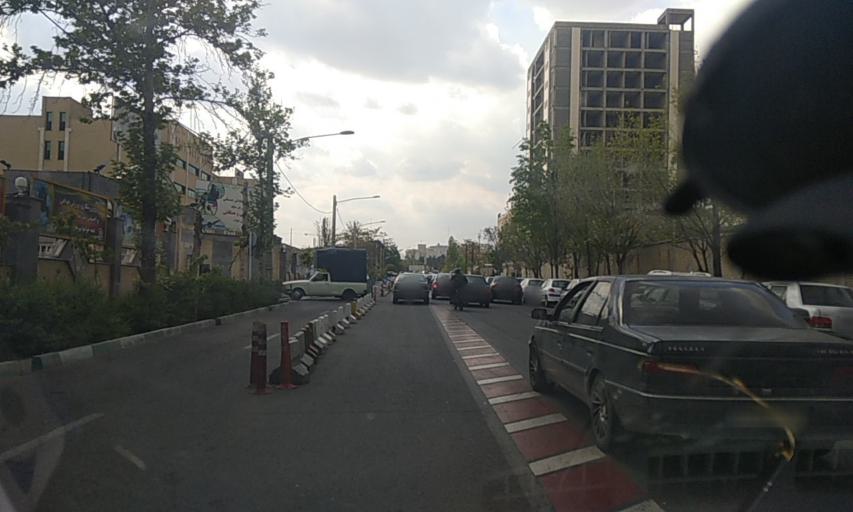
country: IR
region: Tehran
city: Tajrish
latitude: 35.7692
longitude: 51.4054
